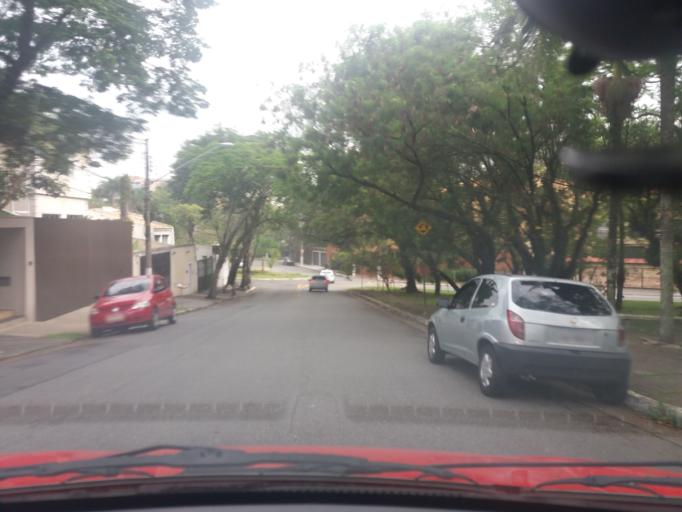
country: BR
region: Sao Paulo
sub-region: Taboao Da Serra
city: Taboao da Serra
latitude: -23.5946
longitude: -46.7155
